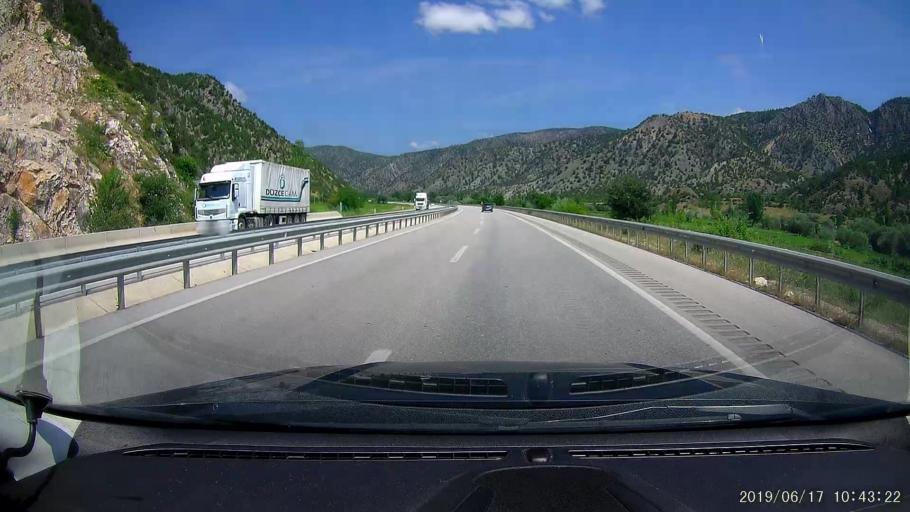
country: TR
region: Corum
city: Kargi
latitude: 41.0635
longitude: 34.5370
